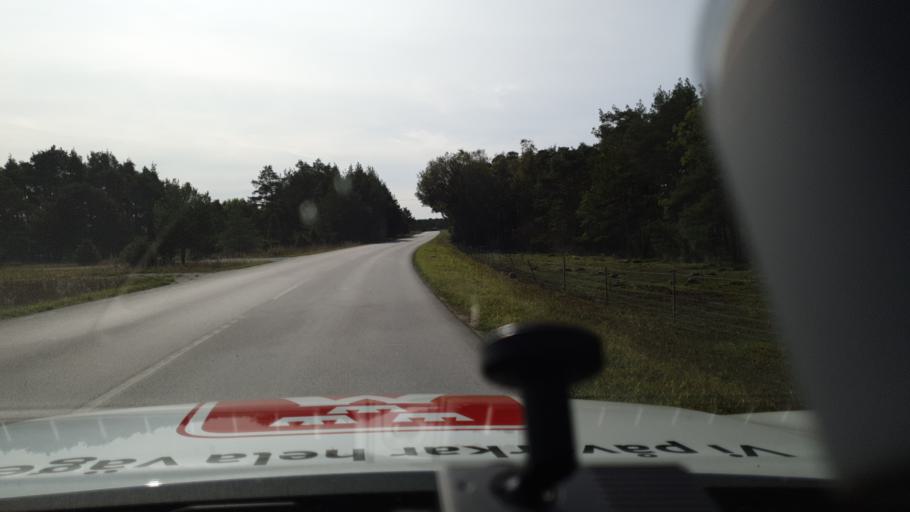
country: SE
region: Gotland
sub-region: Gotland
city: Slite
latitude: 57.8937
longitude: 19.0928
